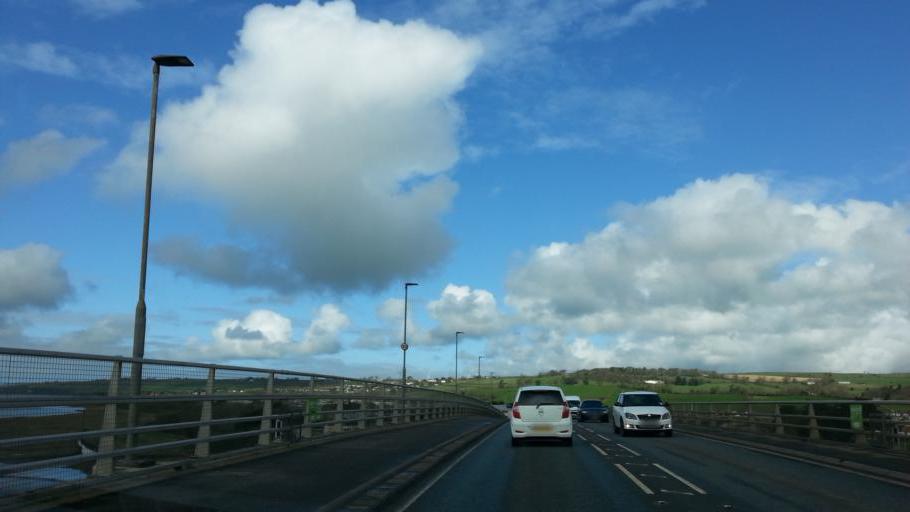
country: GB
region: England
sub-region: Devon
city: Barnstaple
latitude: 51.0795
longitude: -4.0706
